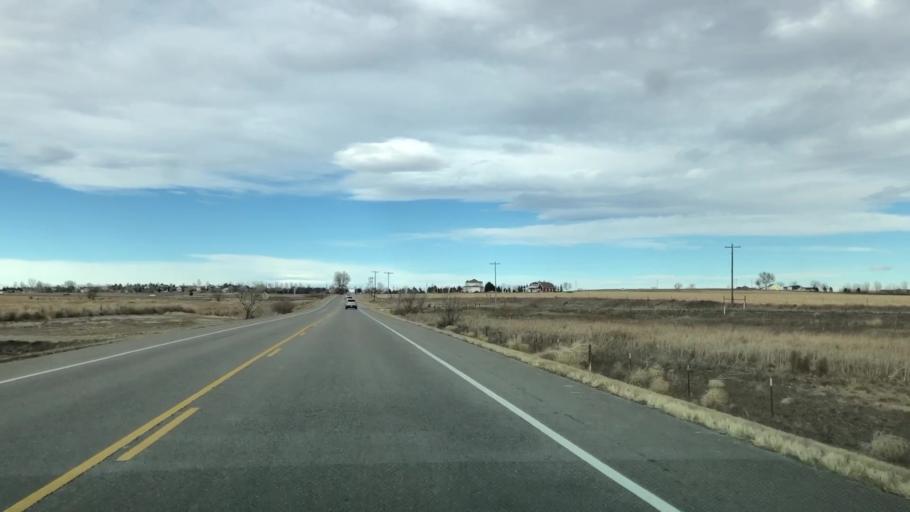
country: US
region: Colorado
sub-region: Weld County
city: Windsor
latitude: 40.5168
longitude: -104.9268
